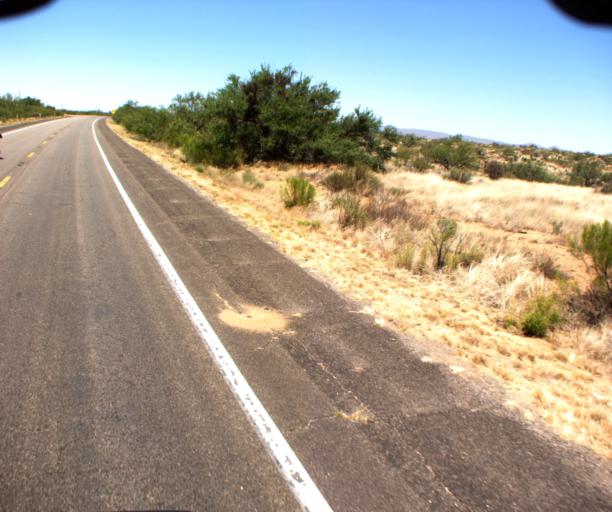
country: US
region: Arizona
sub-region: Pima County
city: Catalina
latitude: 32.5678
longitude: -110.9433
